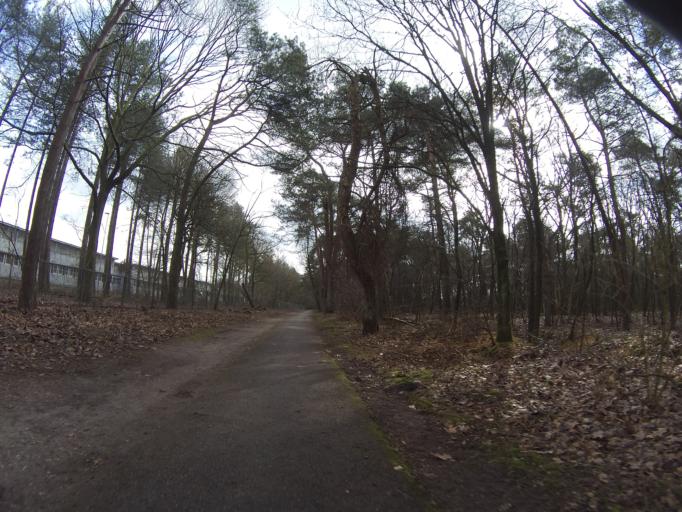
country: NL
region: Utrecht
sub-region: Gemeente Utrechtse Heuvelrug
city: Driebergen-Rijsenburg
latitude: 52.1101
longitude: 5.2902
